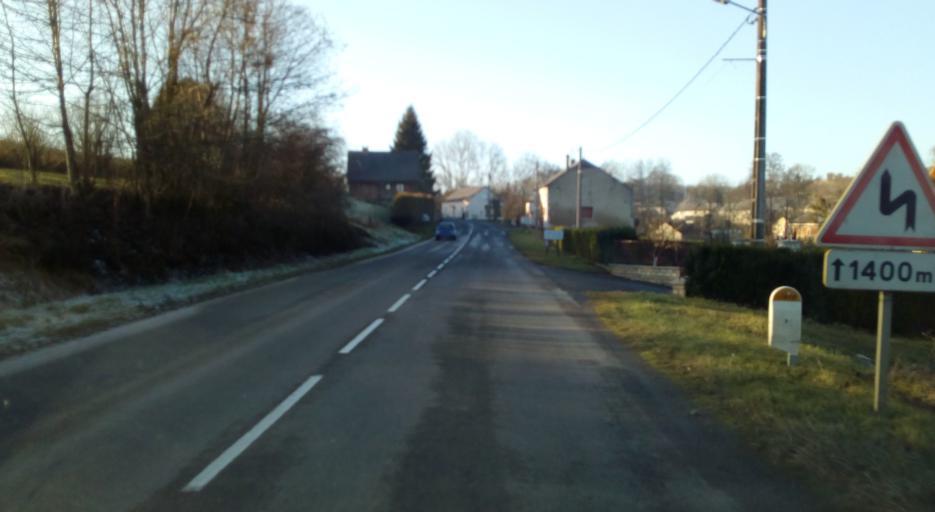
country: FR
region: Champagne-Ardenne
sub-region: Departement des Ardennes
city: Rimogne
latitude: 49.7773
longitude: 4.4055
